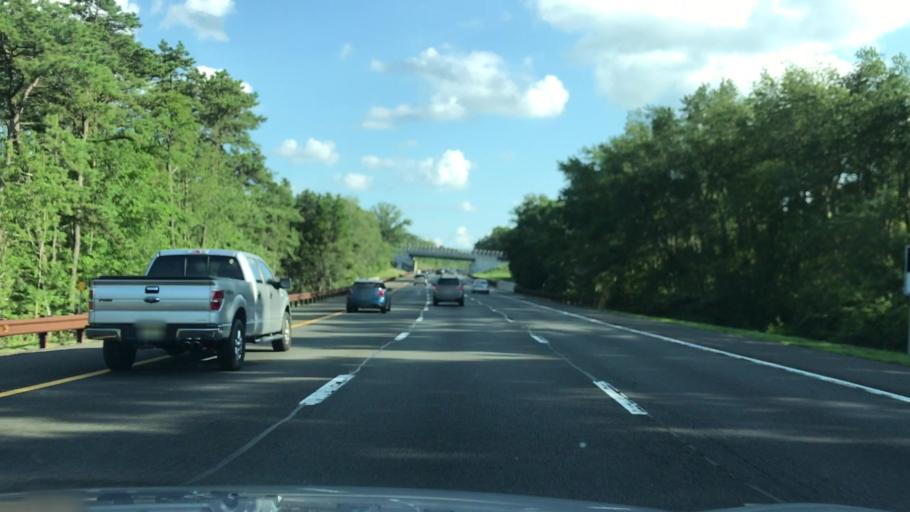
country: US
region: New Jersey
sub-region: Ocean County
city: South Toms River
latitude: 39.9364
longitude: -74.2095
